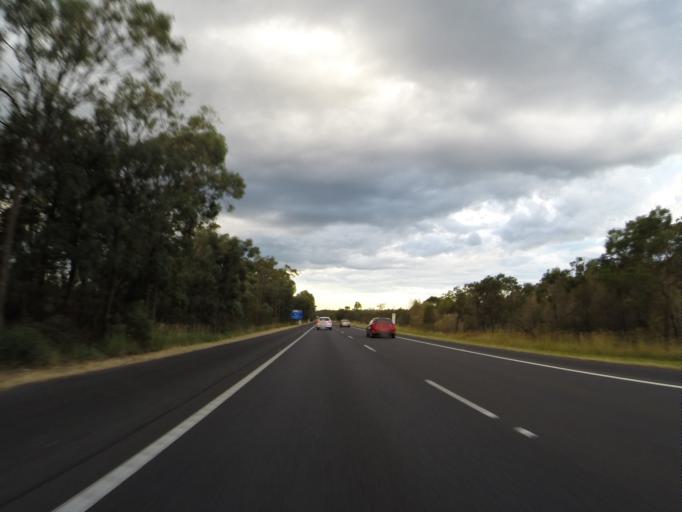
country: AU
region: New South Wales
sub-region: Wollondilly
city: Buxton
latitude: -34.2934
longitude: 150.6228
